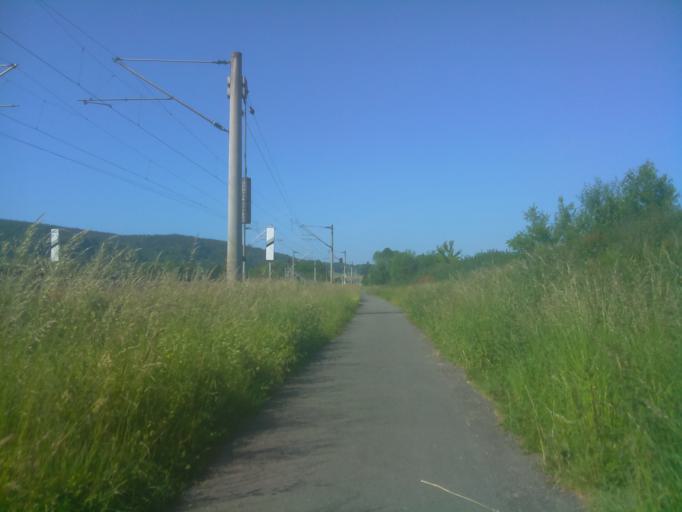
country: DE
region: Thuringia
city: Orlamunde
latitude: 50.7454
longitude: 11.4807
